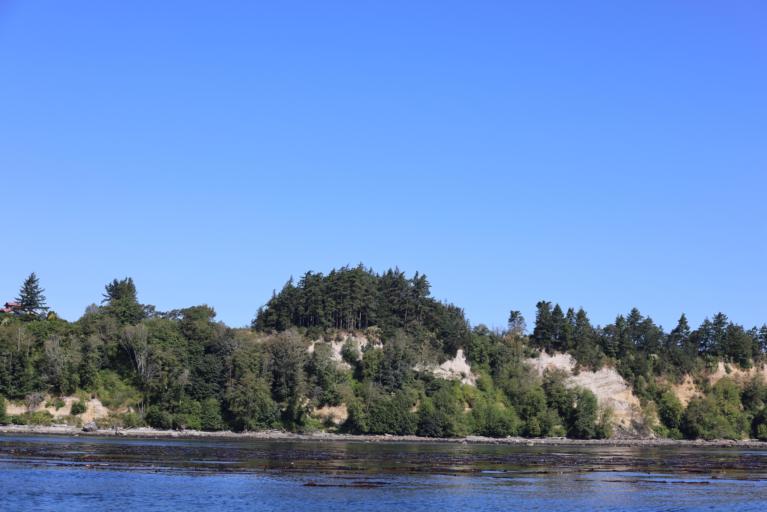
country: CA
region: British Columbia
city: Metchosin
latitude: 48.3736
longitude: -123.5177
